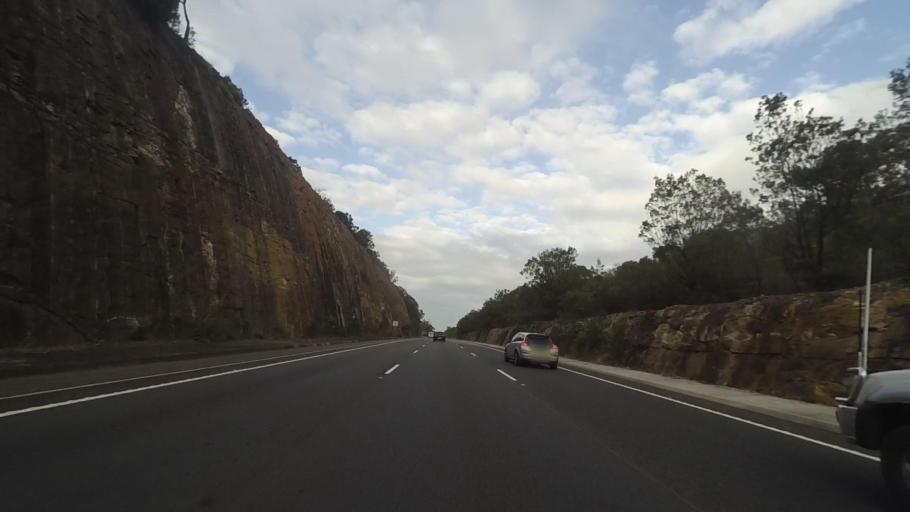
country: AU
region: New South Wales
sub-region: Wollongong
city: Bulli
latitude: -34.2979
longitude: 150.9132
